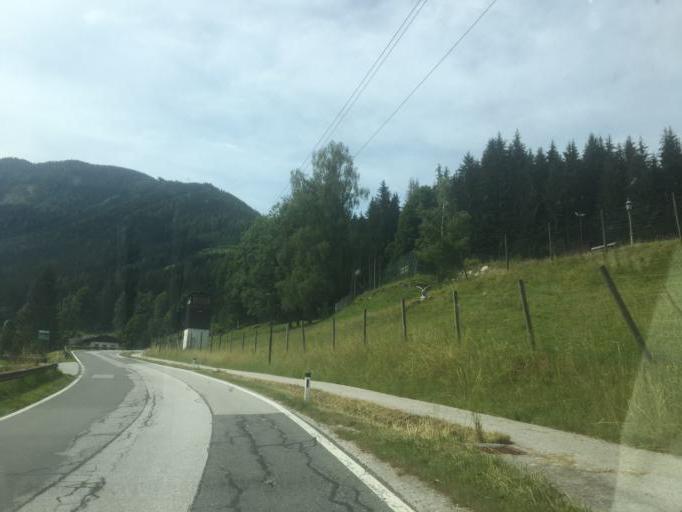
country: AT
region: Styria
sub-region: Politischer Bezirk Liezen
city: Schladming
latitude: 47.3715
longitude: 13.6763
